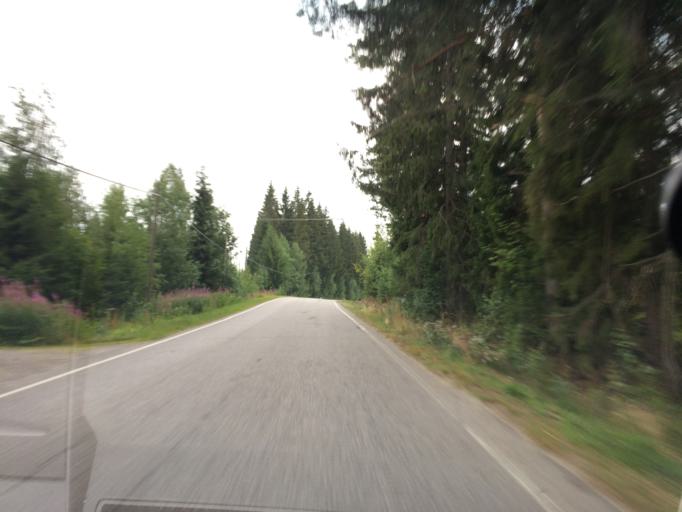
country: FI
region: Haeme
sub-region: Haemeenlinna
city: Tuulos
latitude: 61.1967
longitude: 24.7401
